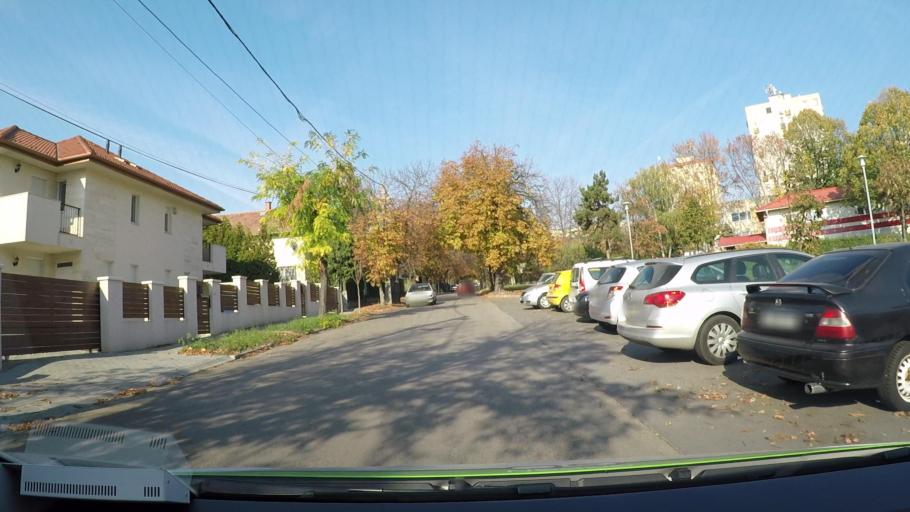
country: HU
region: Budapest
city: Budapest XXII. keruelet
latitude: 47.4129
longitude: 19.0319
